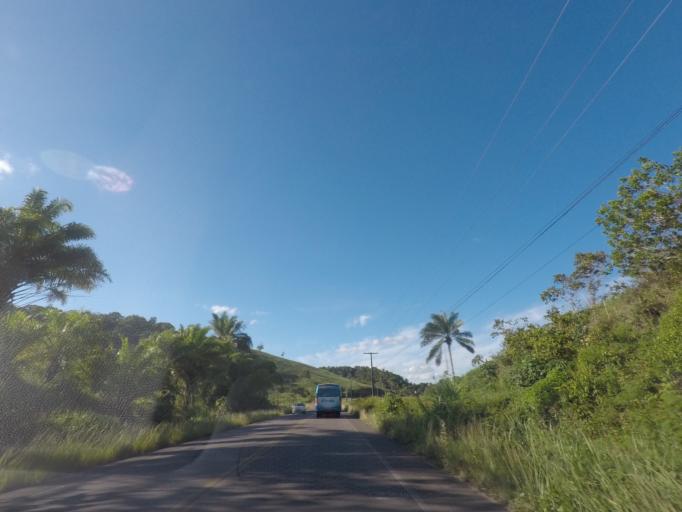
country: BR
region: Bahia
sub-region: Nazare
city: Nazare
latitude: -13.0520
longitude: -39.0060
